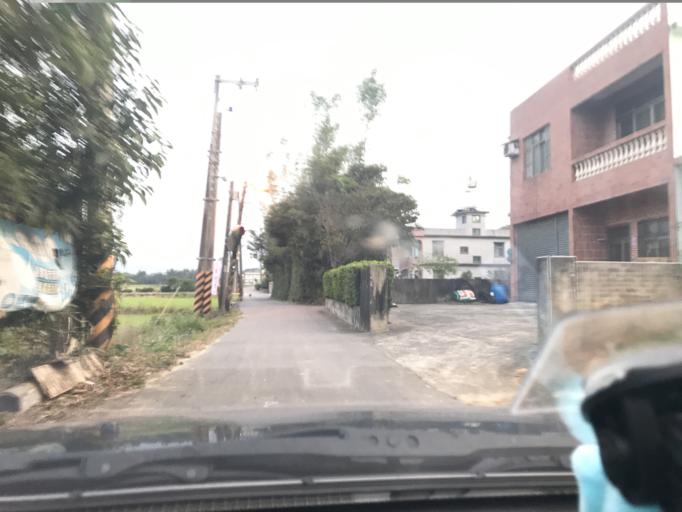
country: TW
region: Taiwan
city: Daxi
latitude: 24.8488
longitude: 121.2099
